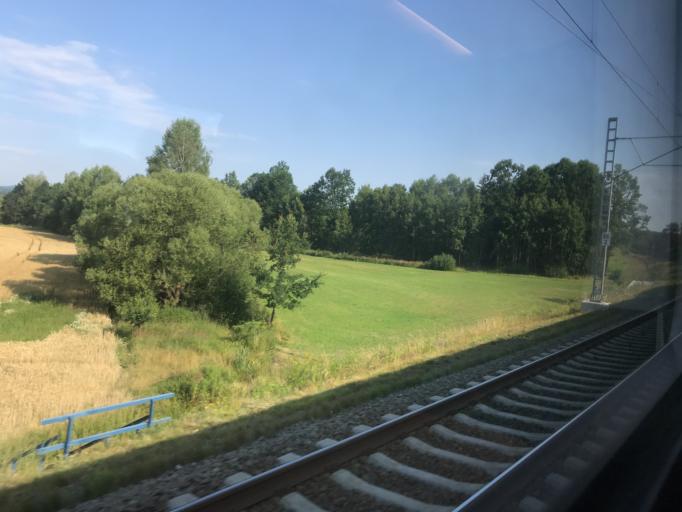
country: CZ
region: Jihocesky
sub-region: Okres Tabor
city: Tabor
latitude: 49.4387
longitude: 14.6899
